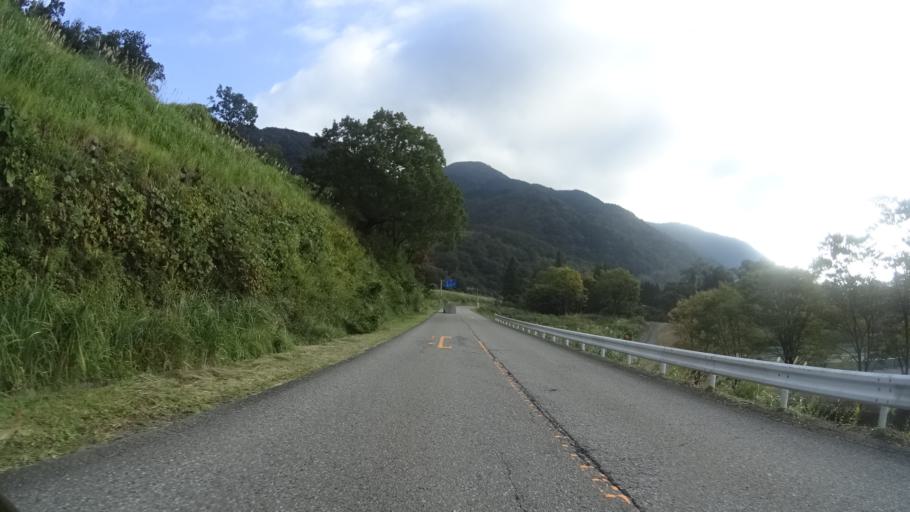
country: JP
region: Oita
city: Beppu
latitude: 33.2606
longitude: 131.3808
